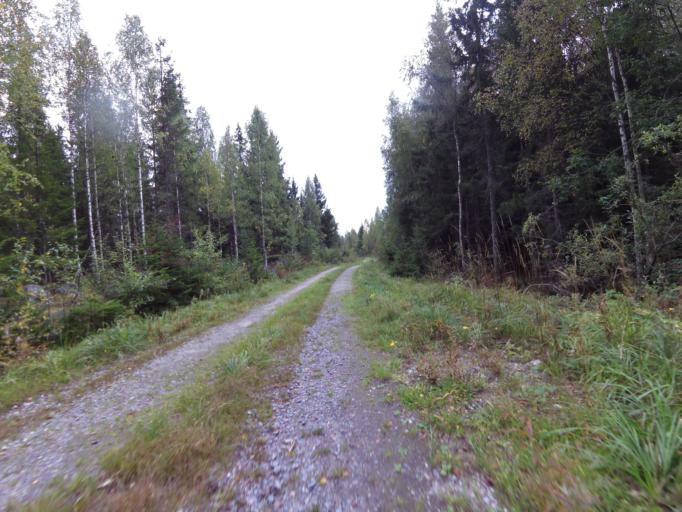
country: SE
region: Gaevleborg
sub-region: Gavle Kommun
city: Valbo
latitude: 60.7233
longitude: 17.0347
